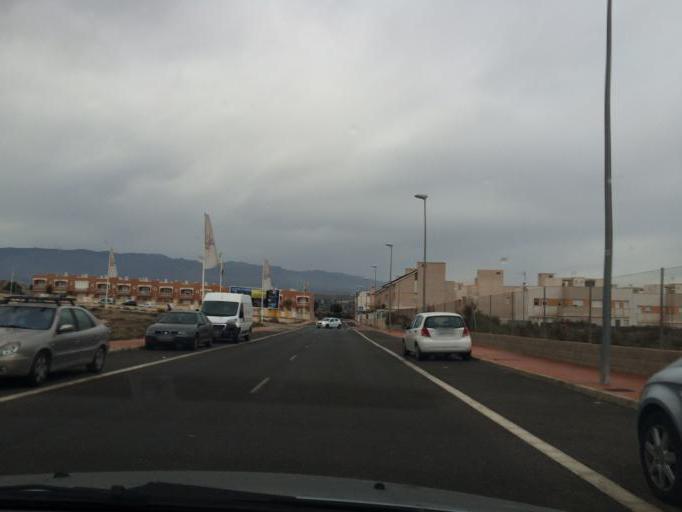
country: ES
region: Andalusia
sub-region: Provincia de Almeria
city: Almeria
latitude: 36.8546
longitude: -2.4380
